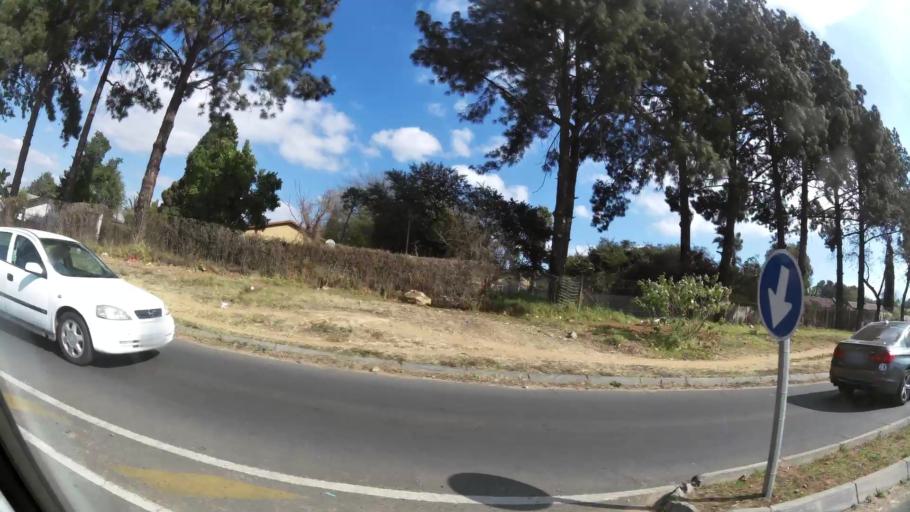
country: ZA
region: Gauteng
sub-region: City of Johannesburg Metropolitan Municipality
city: Midrand
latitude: -25.9841
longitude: 28.1191
